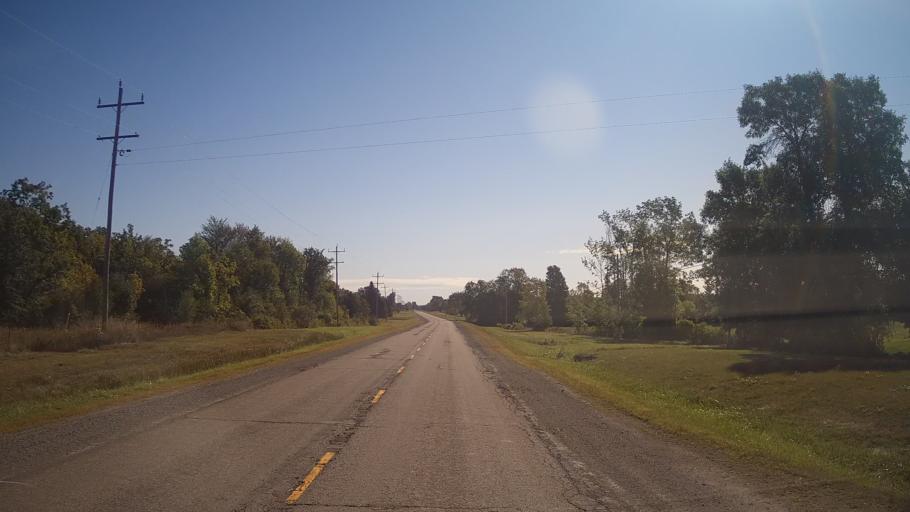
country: CA
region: Ontario
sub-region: Lanark County
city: Smiths Falls
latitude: 44.6264
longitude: -76.0332
